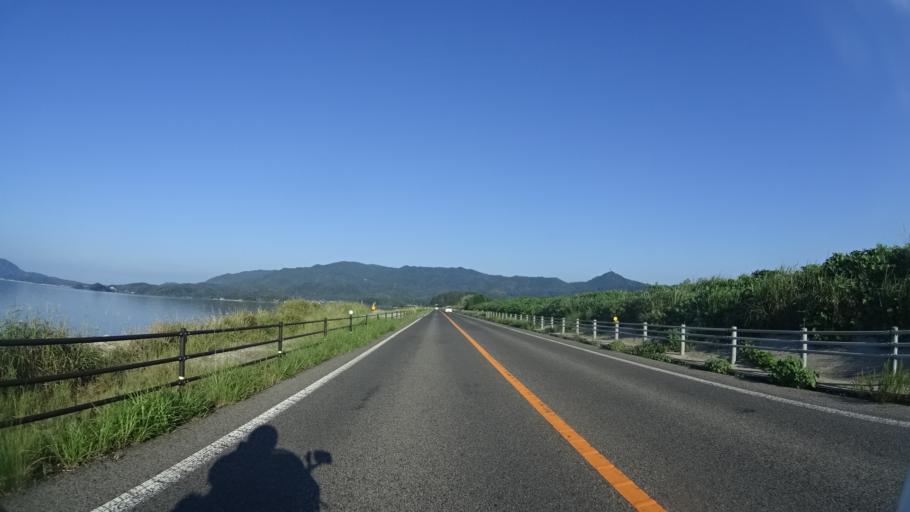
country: JP
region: Shimane
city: Sakaiminato
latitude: 35.5275
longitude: 133.1723
